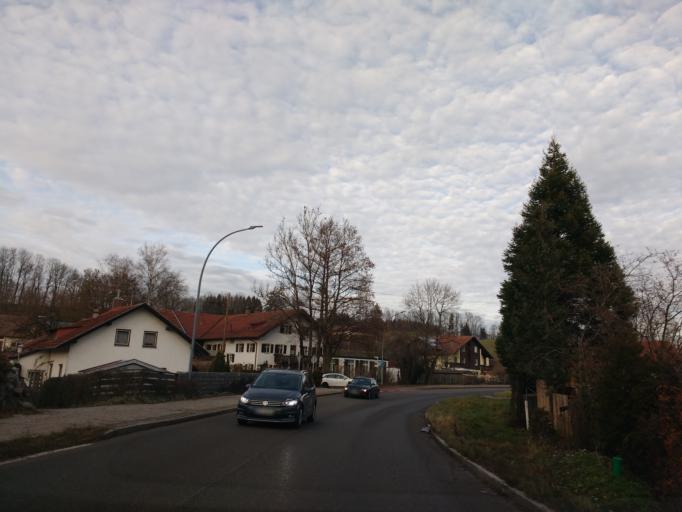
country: DE
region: Bavaria
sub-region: Swabia
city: Neuburg
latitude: 47.7684
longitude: 10.3369
